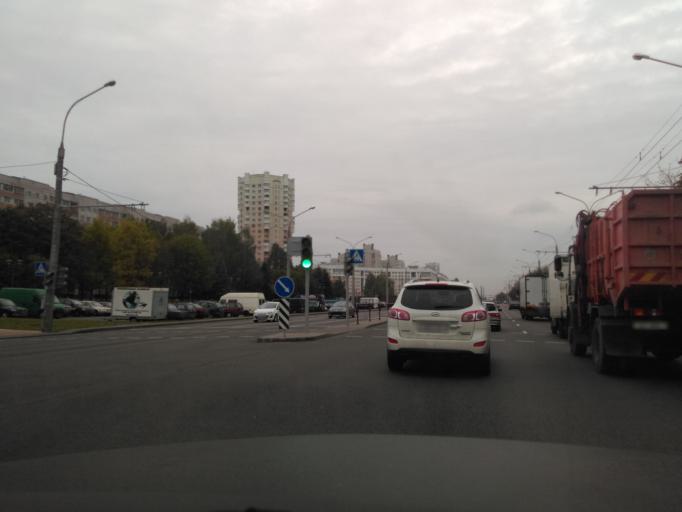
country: BY
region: Minsk
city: Minsk
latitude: 53.8594
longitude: 27.6085
